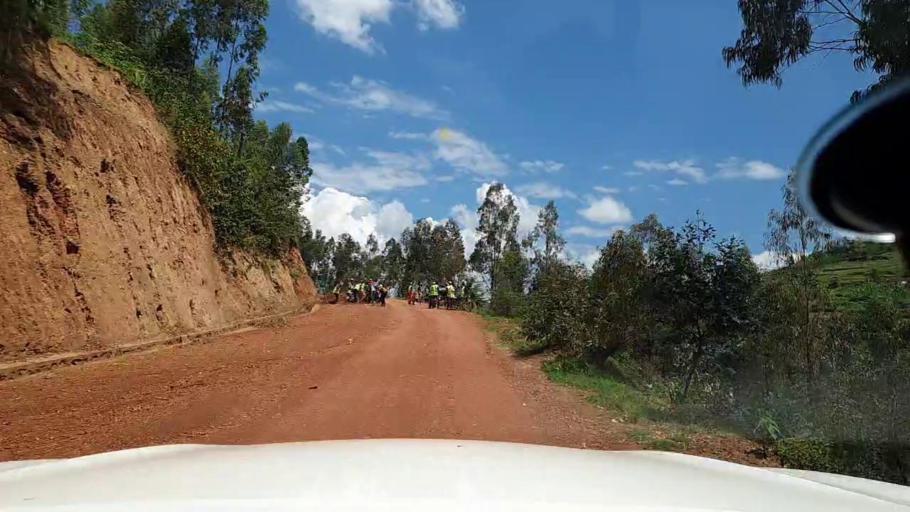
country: RW
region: Northern Province
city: Byumba
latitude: -1.7390
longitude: 29.8621
